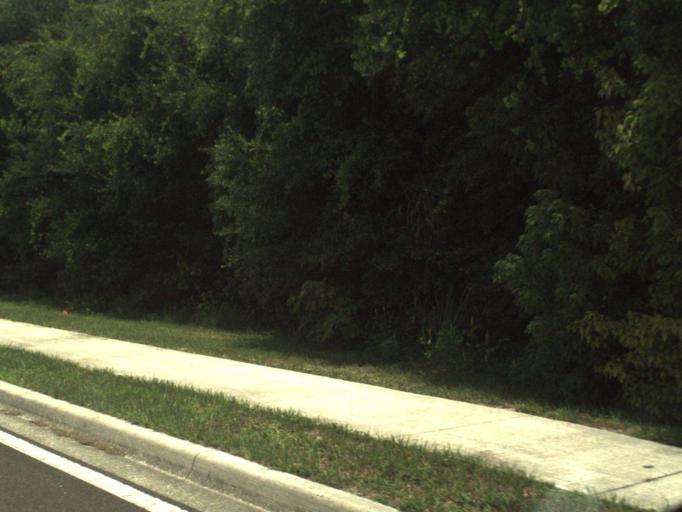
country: US
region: Florida
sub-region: Seminole County
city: Oviedo
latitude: 28.6315
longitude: -81.2403
